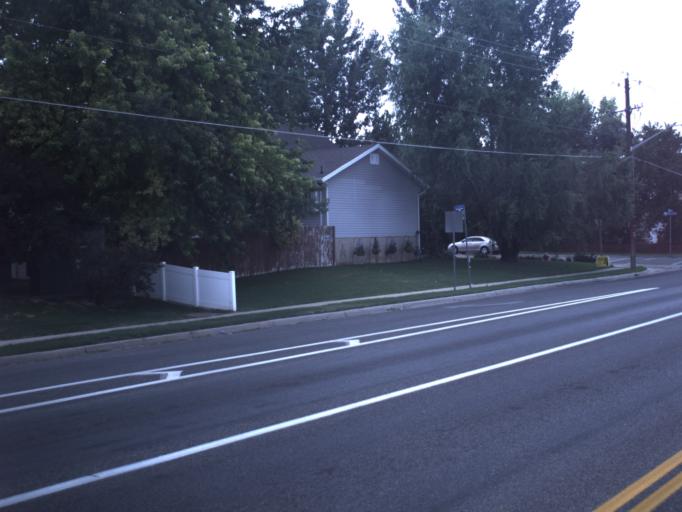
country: US
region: Utah
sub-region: Weber County
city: West Haven
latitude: 41.1758
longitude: -112.0645
